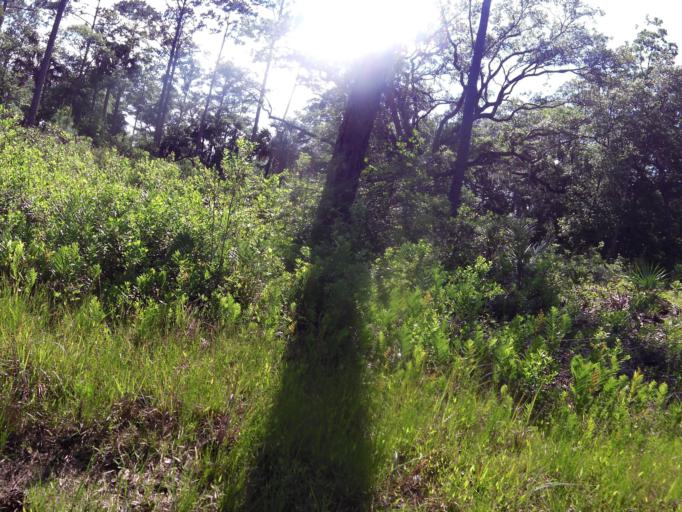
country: US
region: Florida
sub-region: Saint Johns County
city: Palm Valley
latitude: 30.1372
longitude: -81.3711
